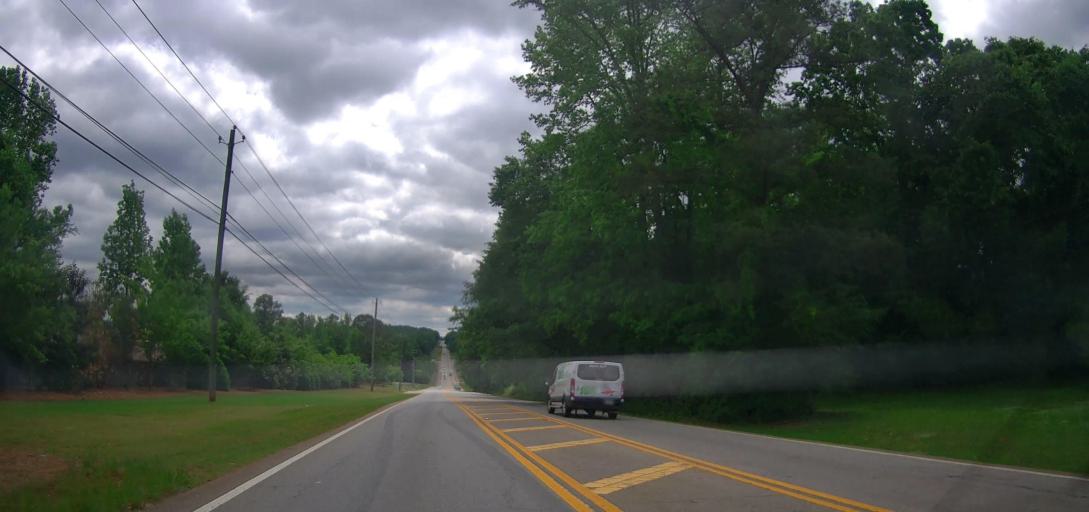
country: US
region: Georgia
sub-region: Henry County
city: Stockbridge
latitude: 33.5544
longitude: -84.1743
